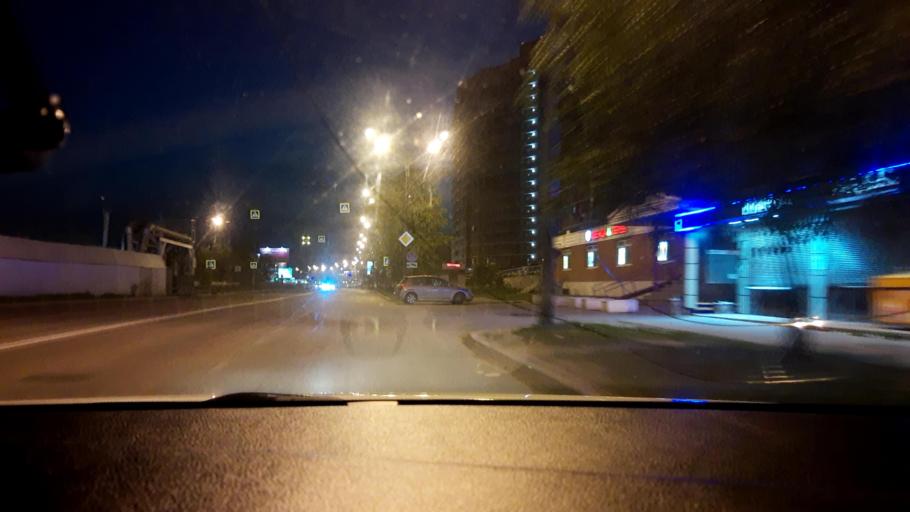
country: RU
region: Moskovskaya
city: Vidnoye
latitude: 55.5426
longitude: 37.7201
